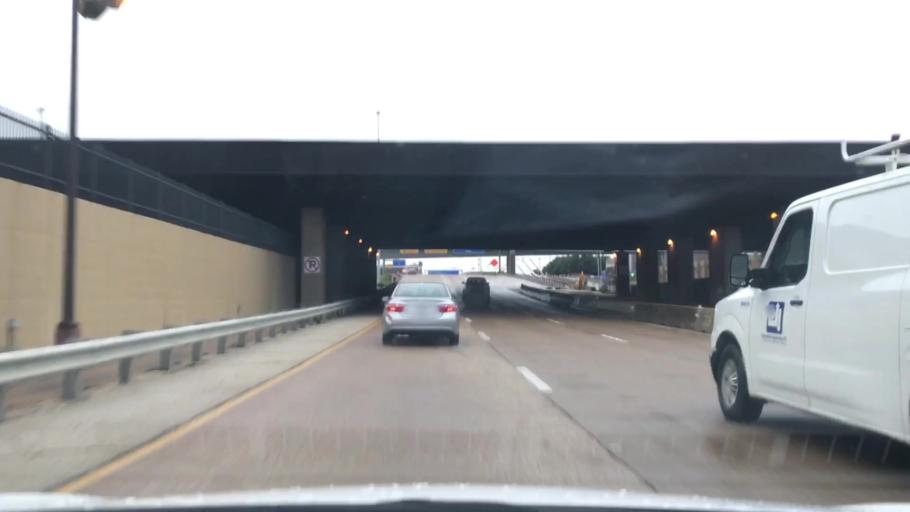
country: US
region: Texas
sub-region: Tarrant County
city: Grapevine
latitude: 32.9097
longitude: -97.0408
